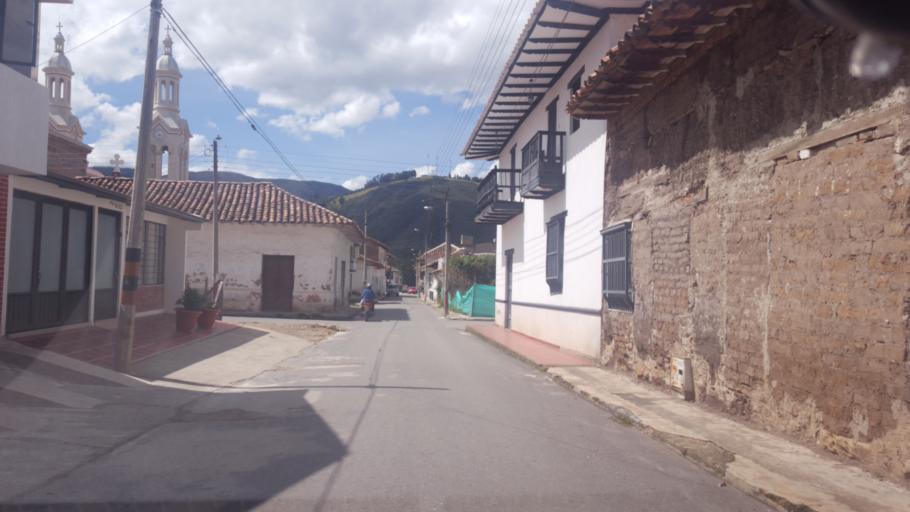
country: CO
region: Boyaca
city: Belen
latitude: 5.9906
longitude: -72.9143
